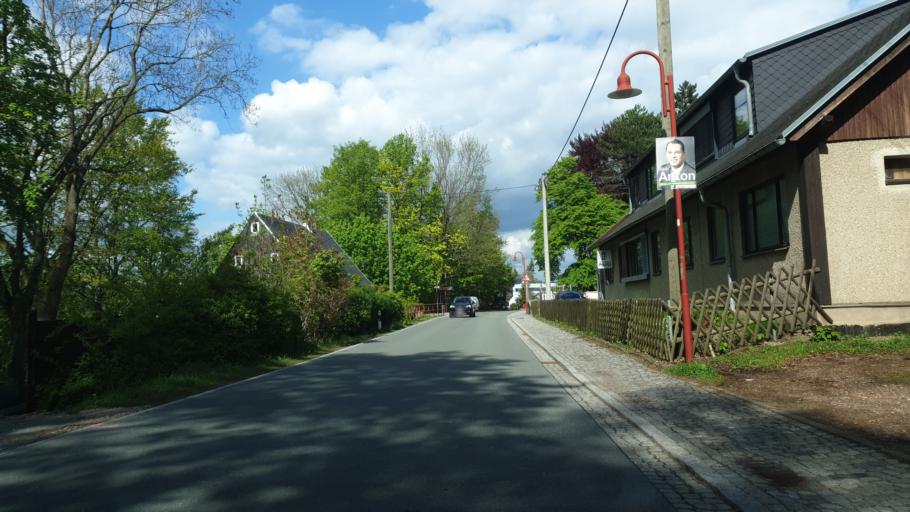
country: DE
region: Saxony
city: Lugau
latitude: 50.7191
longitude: 12.7459
